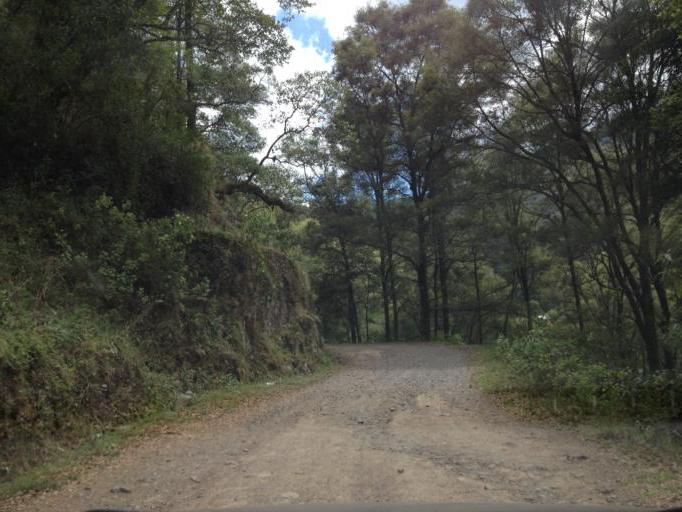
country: MX
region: Hidalgo
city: Mineral del Monte
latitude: 20.2007
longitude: -98.6712
